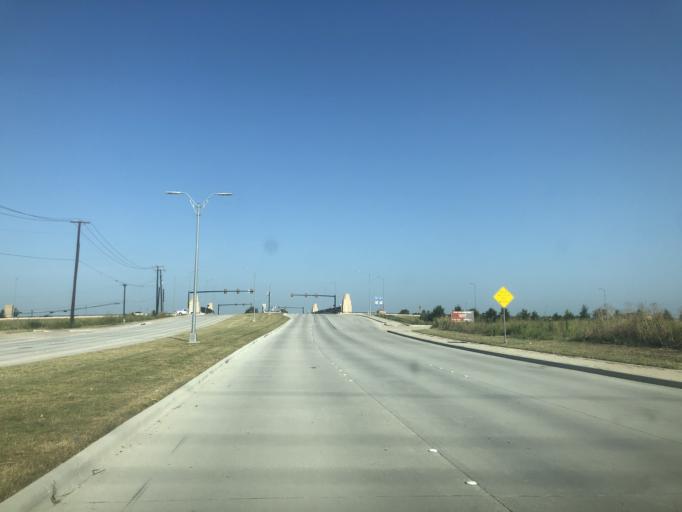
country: US
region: Texas
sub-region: Tarrant County
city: Benbrook
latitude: 32.6449
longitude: -97.4137
